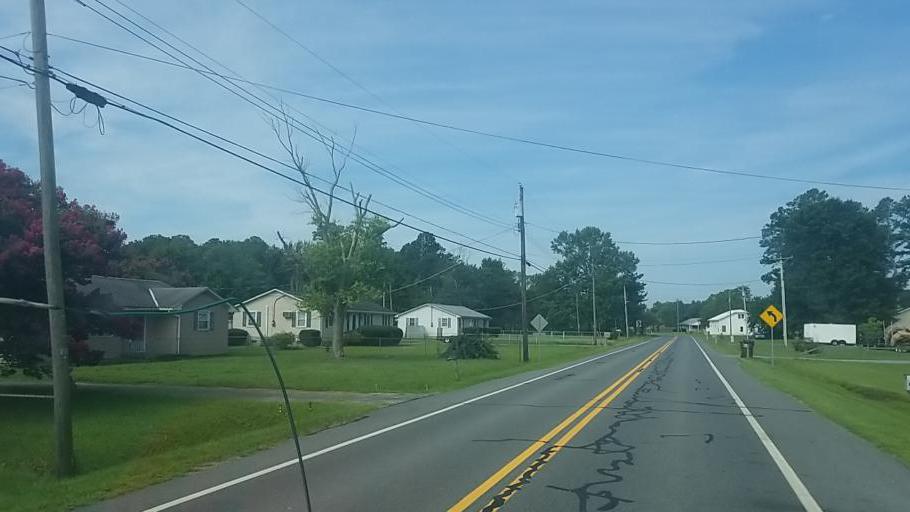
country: US
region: Delaware
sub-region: Sussex County
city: Selbyville
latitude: 38.5255
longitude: -75.2172
